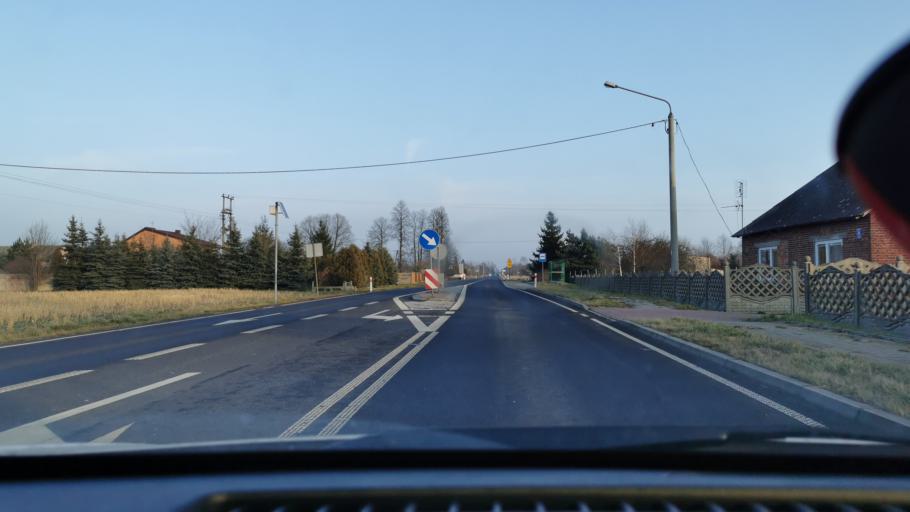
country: PL
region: Lodz Voivodeship
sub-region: Powiat belchatowski
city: Druzbice
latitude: 51.5105
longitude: 19.3715
